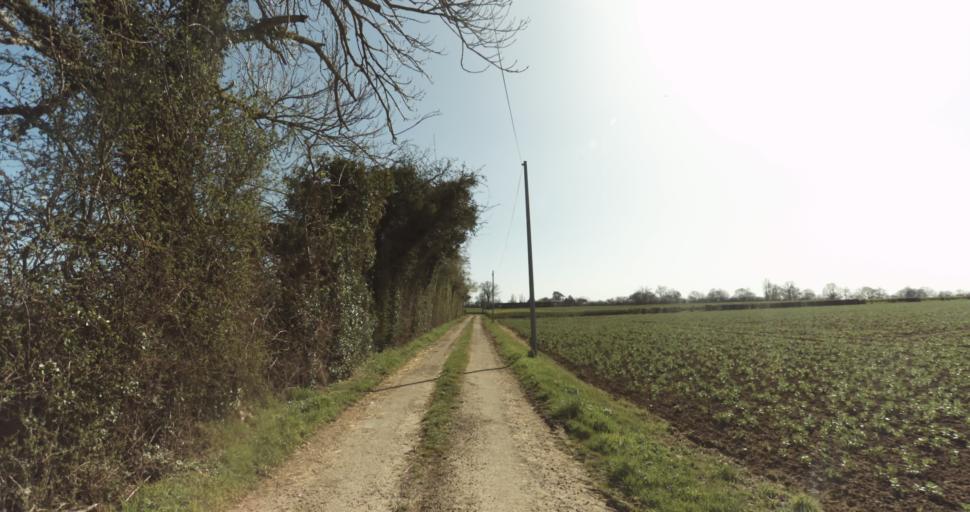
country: FR
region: Lower Normandy
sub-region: Departement du Calvados
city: Saint-Pierre-sur-Dives
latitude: 48.9338
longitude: -0.0056
